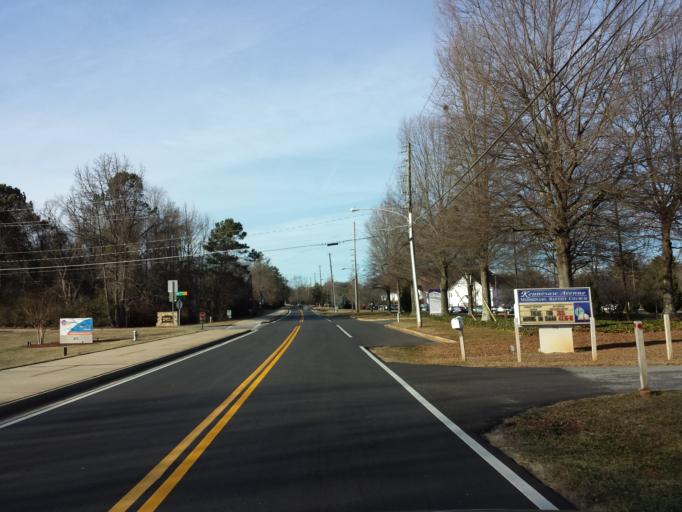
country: US
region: Georgia
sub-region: Cobb County
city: Marietta
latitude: 33.9721
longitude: -84.5645
